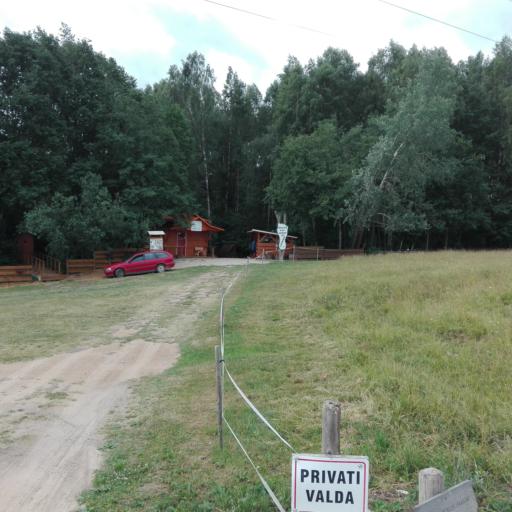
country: LT
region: Panevezys
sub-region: Birzai
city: Birzai
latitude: 56.2351
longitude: 24.7855
